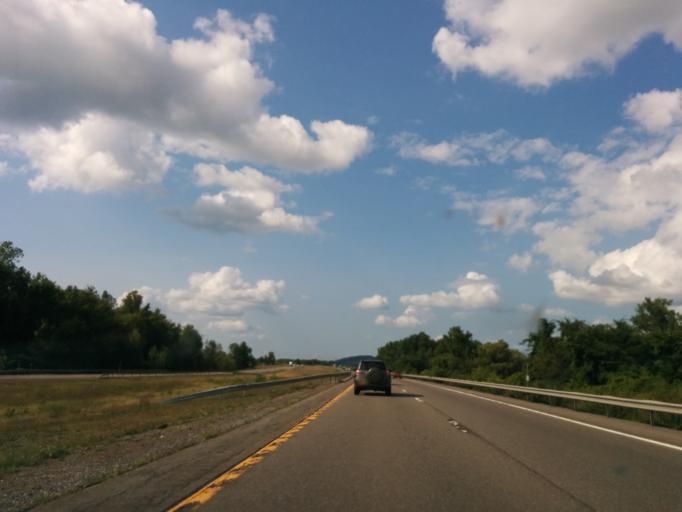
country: US
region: New York
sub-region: Cortland County
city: Homer
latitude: 42.7747
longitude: -76.1270
